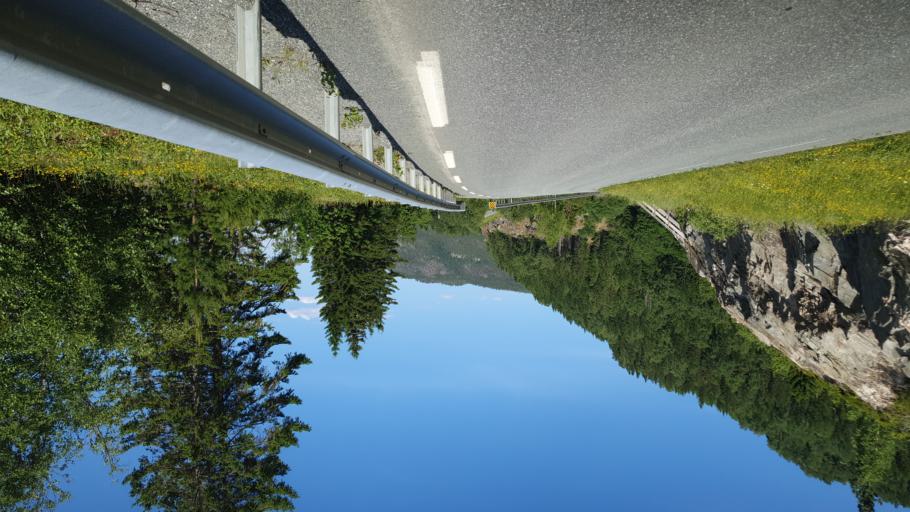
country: NO
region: Nord-Trondelag
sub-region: Leksvik
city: Leksvik
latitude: 63.6122
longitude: 10.5073
